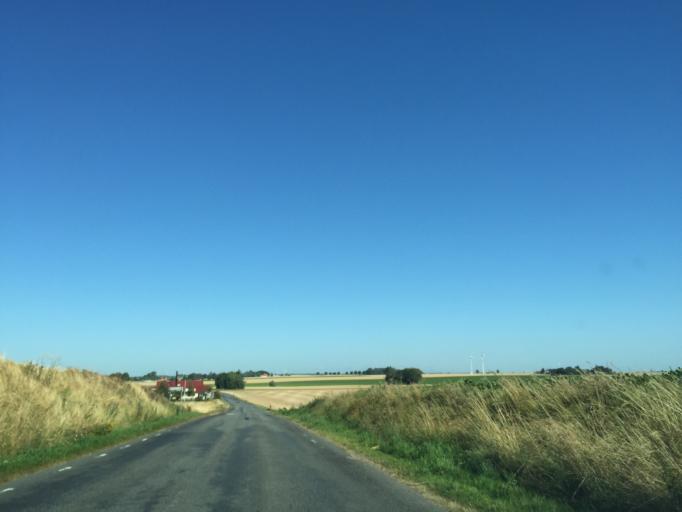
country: SE
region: Skane
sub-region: Ystads Kommun
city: Kopingebro
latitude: 55.4464
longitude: 14.1212
